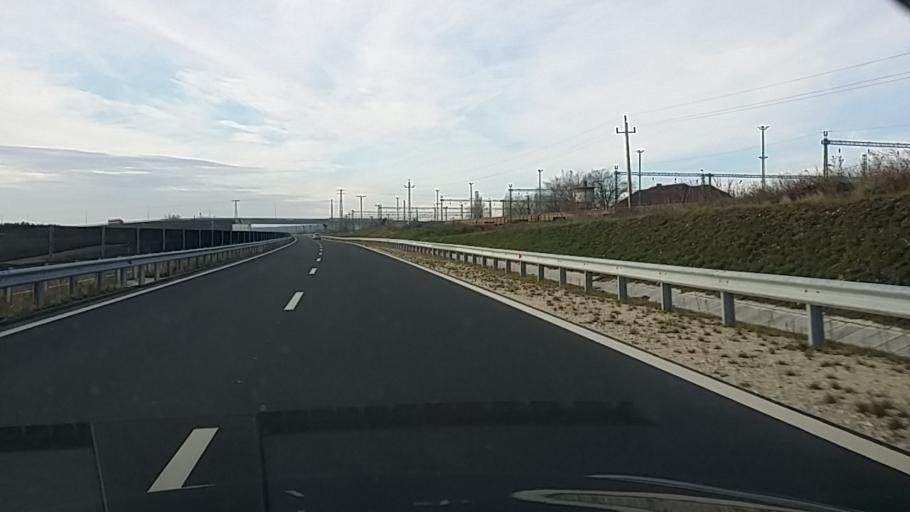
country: HU
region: Veszprem
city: Varpalota
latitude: 47.1951
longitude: 18.1520
